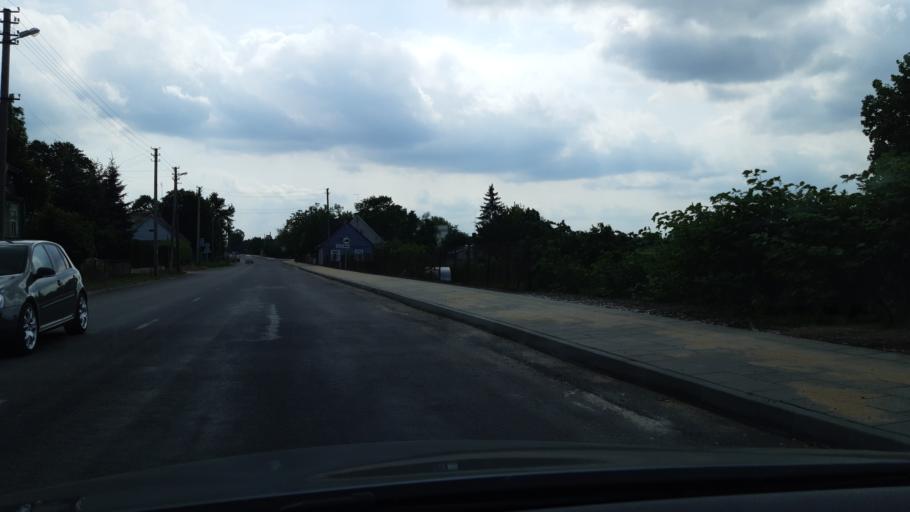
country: LT
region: Kauno apskritis
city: Kedainiai
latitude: 55.2821
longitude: 23.9819
